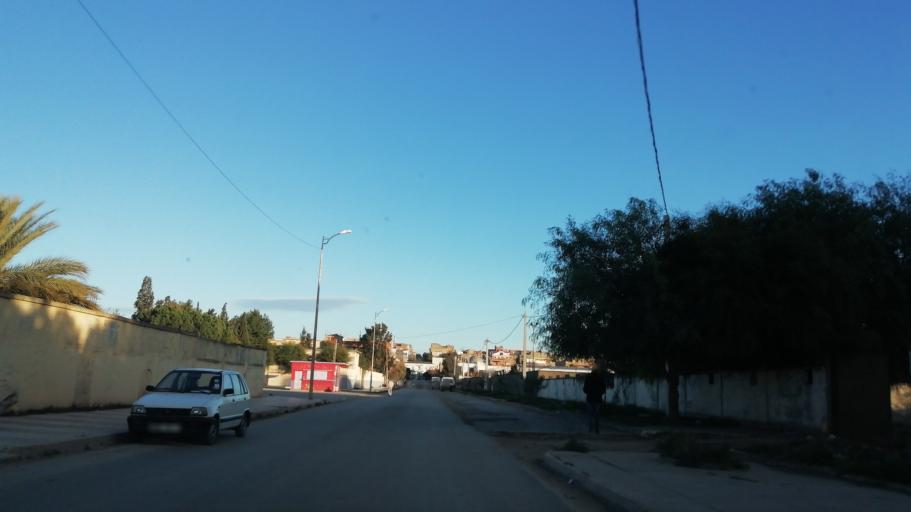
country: DZ
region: Oran
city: Sidi ech Chahmi
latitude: 35.6932
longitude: -0.5061
